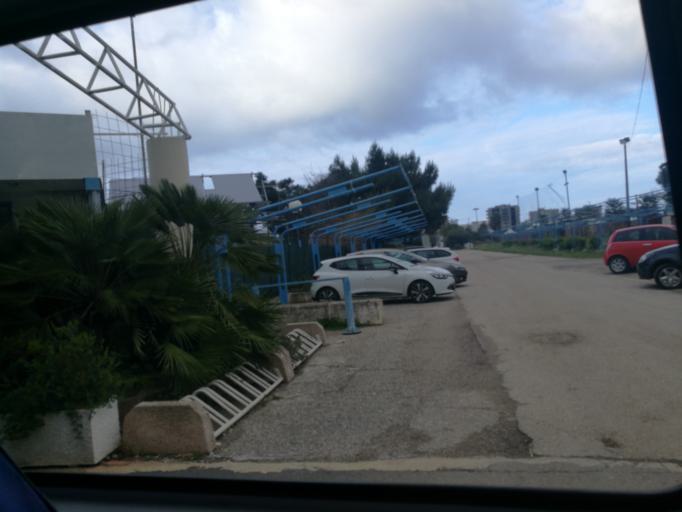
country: IT
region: Apulia
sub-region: Provincia di Bari
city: Triggiano
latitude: 41.0973
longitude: 16.9112
